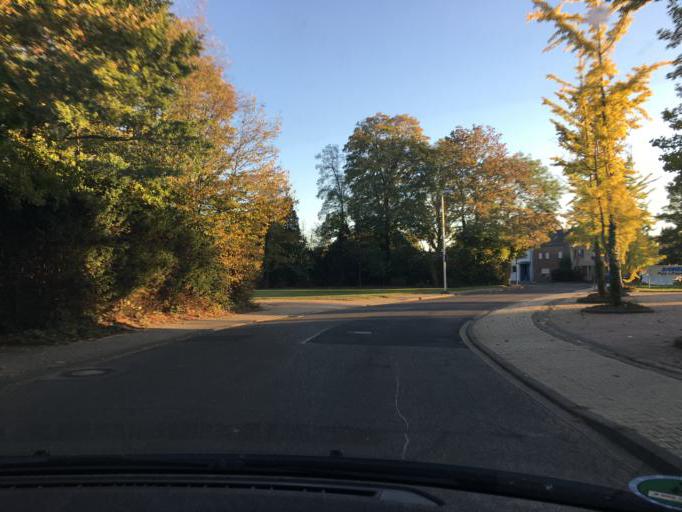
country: DE
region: North Rhine-Westphalia
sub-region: Regierungsbezirk Koln
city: Dueren
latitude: 50.8132
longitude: 6.4451
